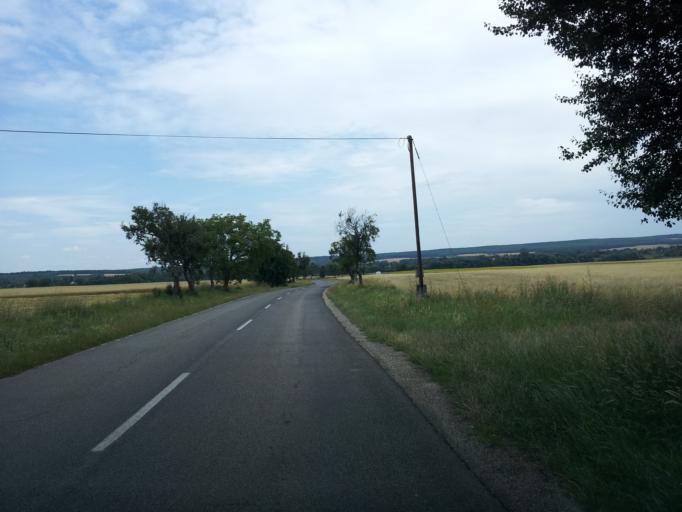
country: HU
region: Vas
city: Vasvar
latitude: 47.0473
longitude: 16.8570
